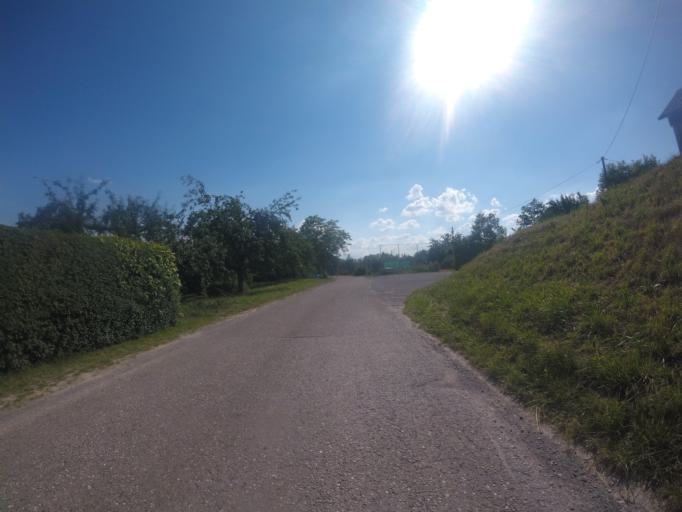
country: DE
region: Baden-Wuerttemberg
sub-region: Regierungsbezirk Stuttgart
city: Oberstenfeld
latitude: 49.0250
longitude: 9.3372
